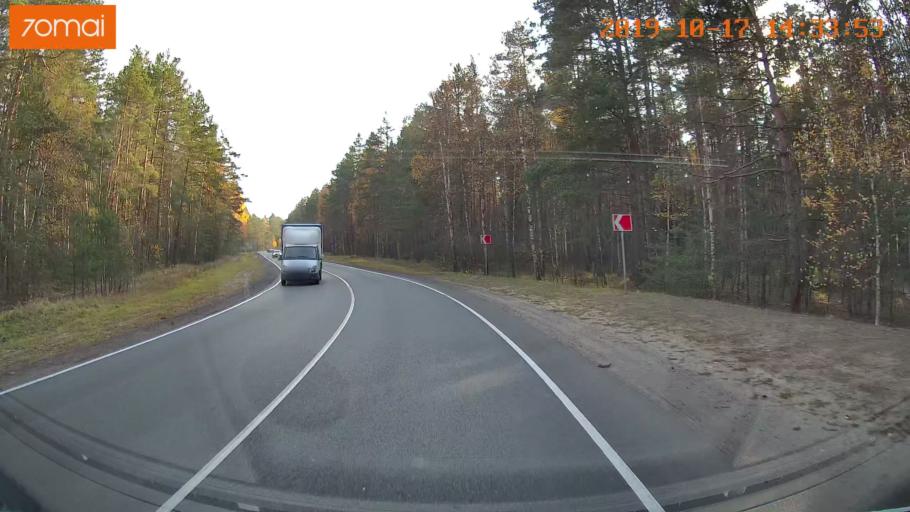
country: RU
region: Rjazan
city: Solotcha
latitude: 54.9189
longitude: 39.9962
